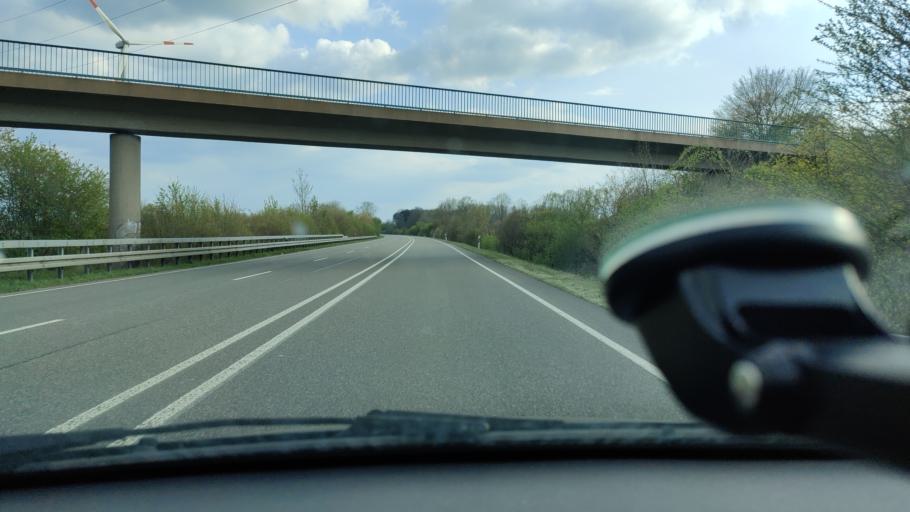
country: DE
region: North Rhine-Westphalia
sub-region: Regierungsbezirk Dusseldorf
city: Bocholt
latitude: 51.7919
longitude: 6.5768
